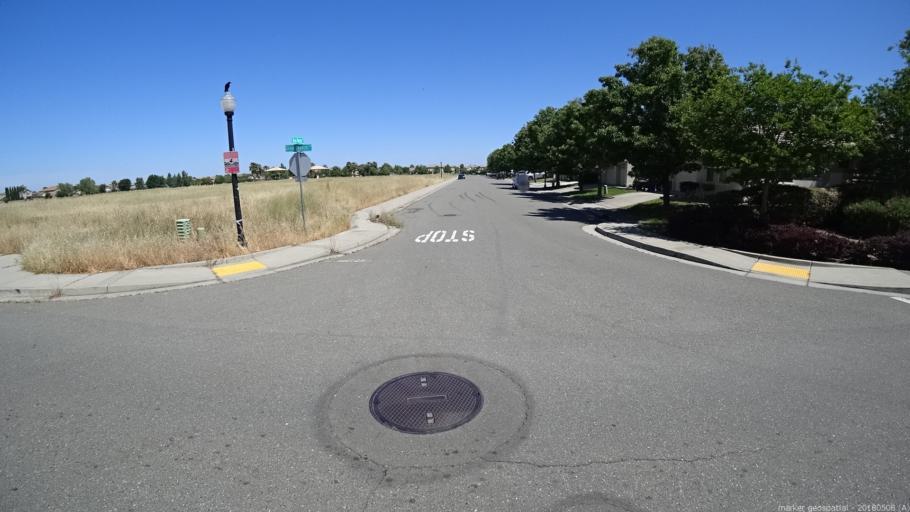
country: US
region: California
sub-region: Sacramento County
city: Elverta
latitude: 38.6780
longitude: -121.5347
